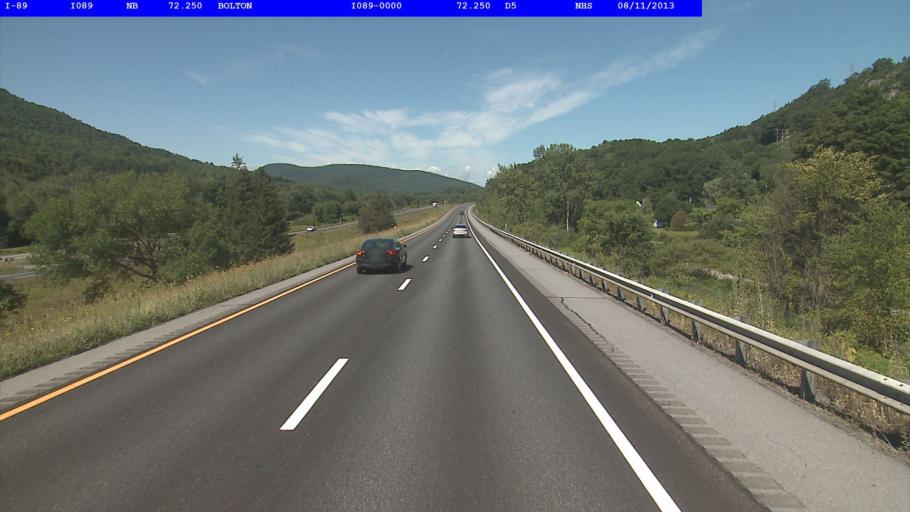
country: US
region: Vermont
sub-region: Chittenden County
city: Jericho
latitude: 44.3800
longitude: -72.9109
